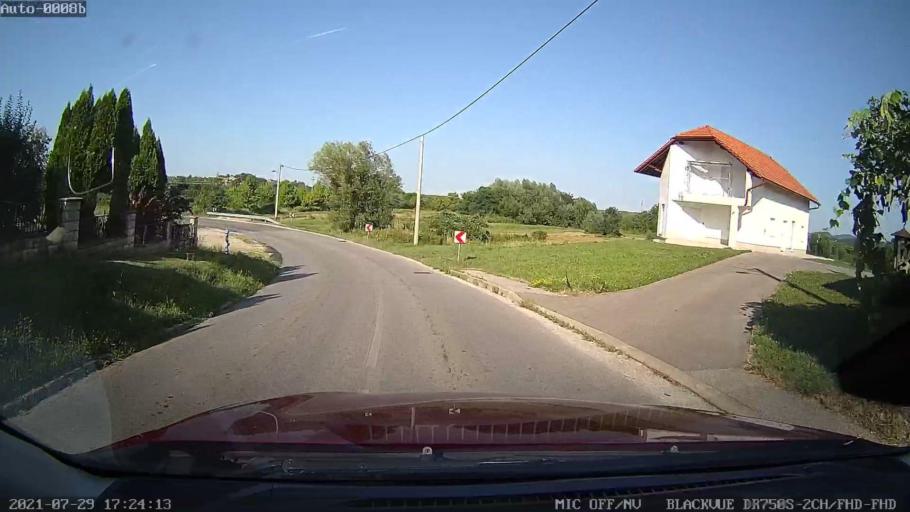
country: HR
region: Varazdinska
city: Ivanec
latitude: 46.2387
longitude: 16.1181
